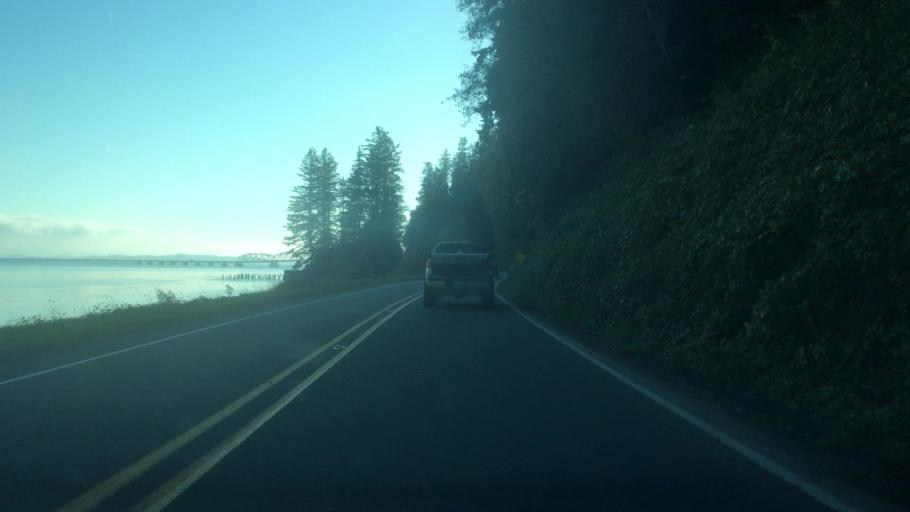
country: US
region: Oregon
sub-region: Clatsop County
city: Astoria
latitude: 46.2482
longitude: -123.8671
